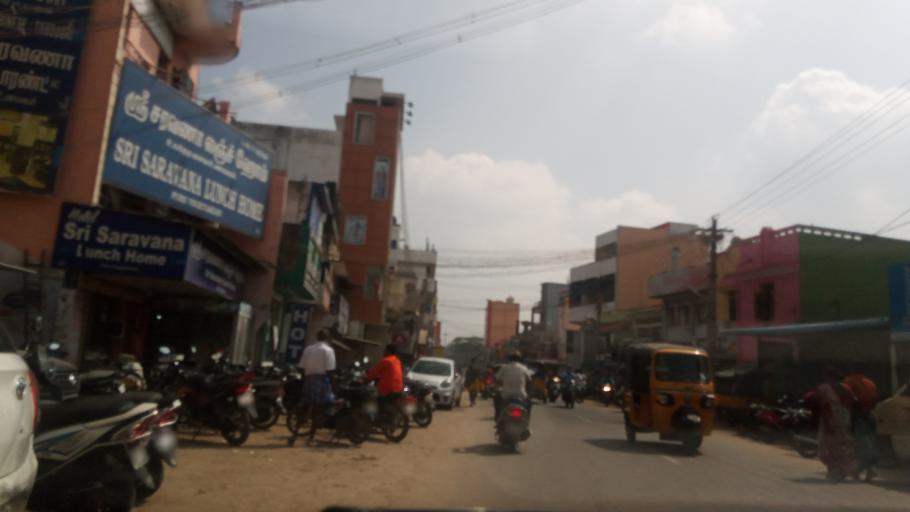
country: IN
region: Tamil Nadu
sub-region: Vellore
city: Arakkonam
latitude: 13.0861
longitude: 79.6629
